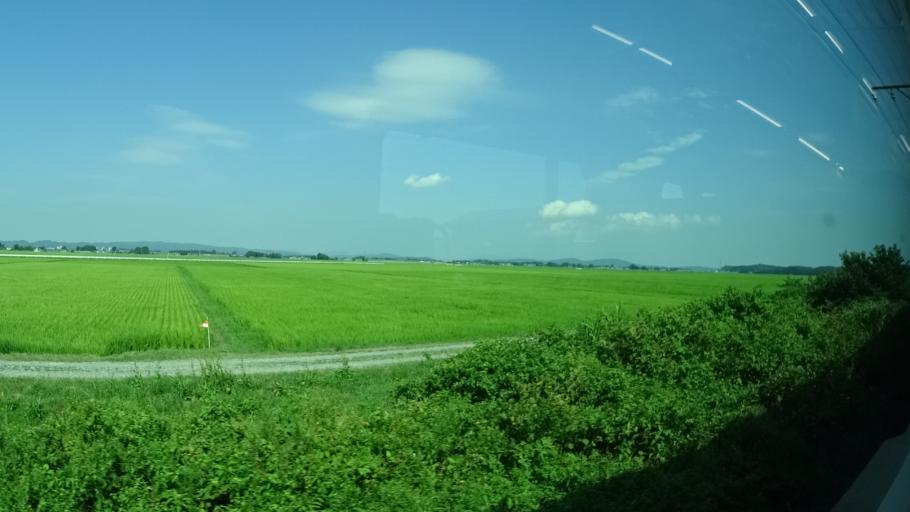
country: JP
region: Miyagi
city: Kogota
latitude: 38.5145
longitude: 141.0738
